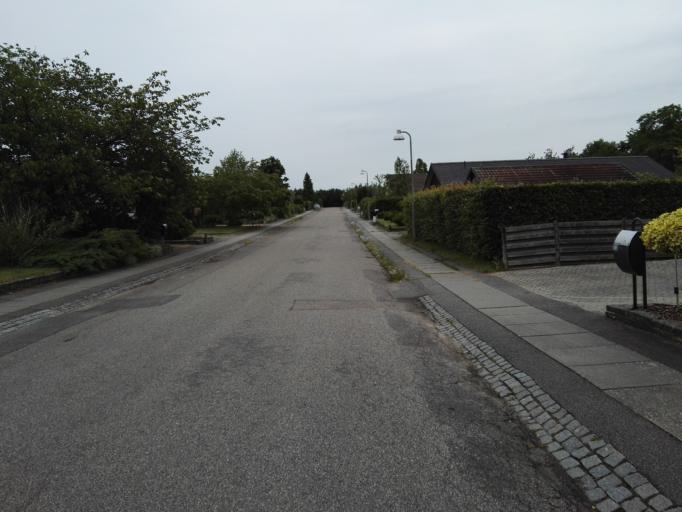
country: DK
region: Zealand
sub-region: Roskilde Kommune
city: Jyllinge
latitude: 55.7452
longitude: 12.1198
